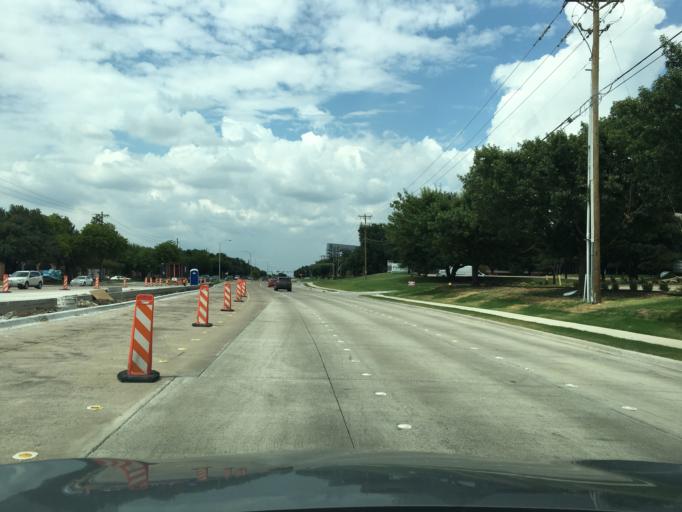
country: US
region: Texas
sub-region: Dallas County
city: Addison
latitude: 33.0173
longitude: -96.7951
